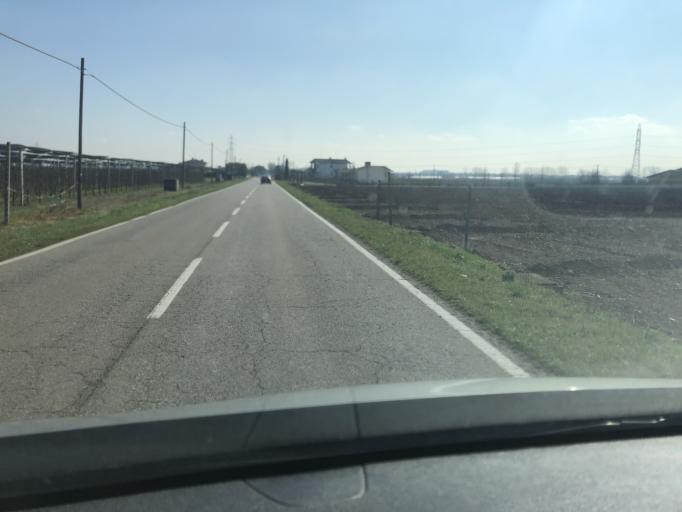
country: IT
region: Veneto
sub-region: Provincia di Verona
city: Villafranca di Verona
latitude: 45.3713
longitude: 10.8316
